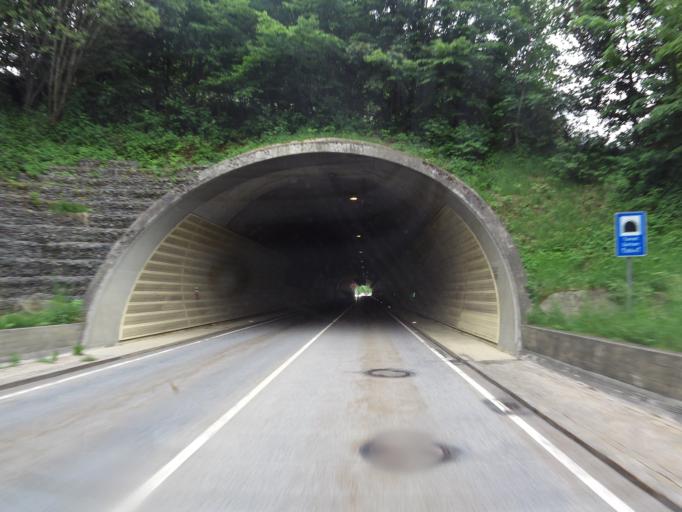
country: DE
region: Bavaria
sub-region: Lower Bavaria
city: Ringelai
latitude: 48.7884
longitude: 13.5063
